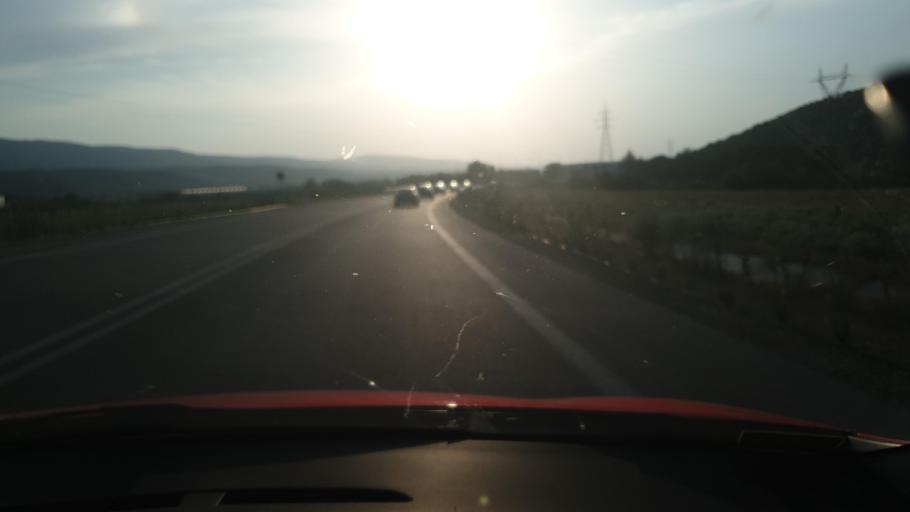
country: GR
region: Central Macedonia
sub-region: Nomos Thessalonikis
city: Vasilika
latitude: 40.4660
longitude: 23.2026
